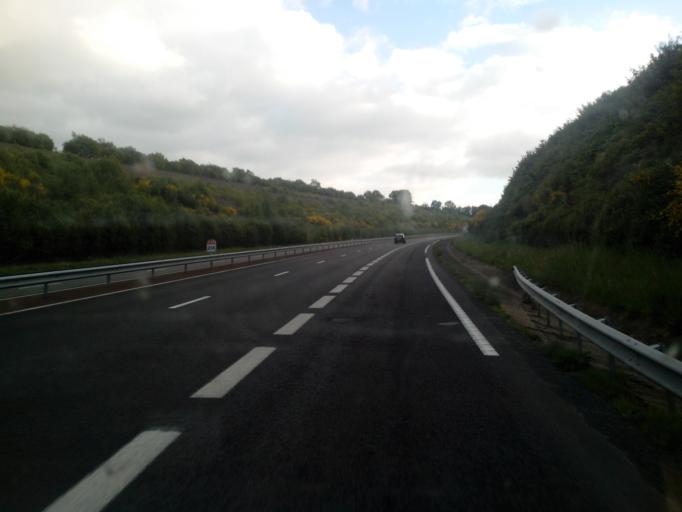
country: FR
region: Lower Normandy
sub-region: Departement de la Manche
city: Tessy-sur-Vire
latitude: 48.9269
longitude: -1.0756
